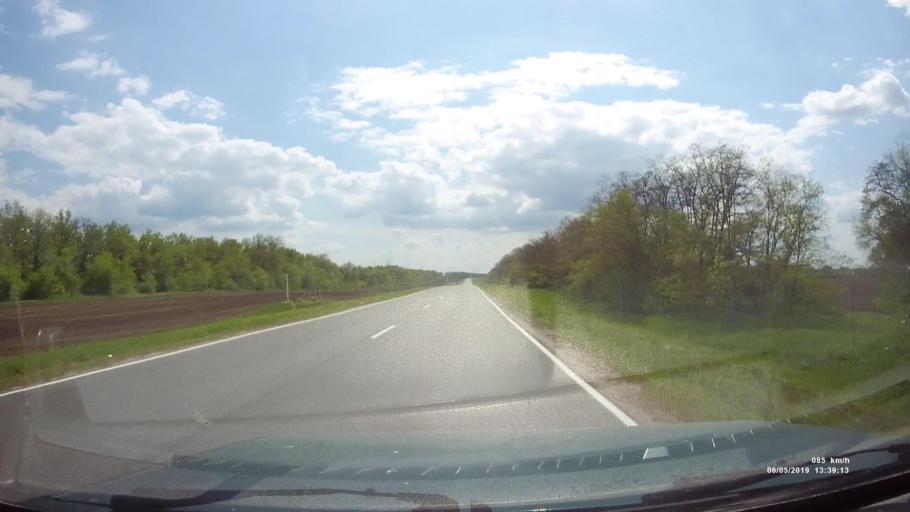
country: RU
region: Rostov
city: Ust'-Donetskiy
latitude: 47.6785
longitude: 40.7046
